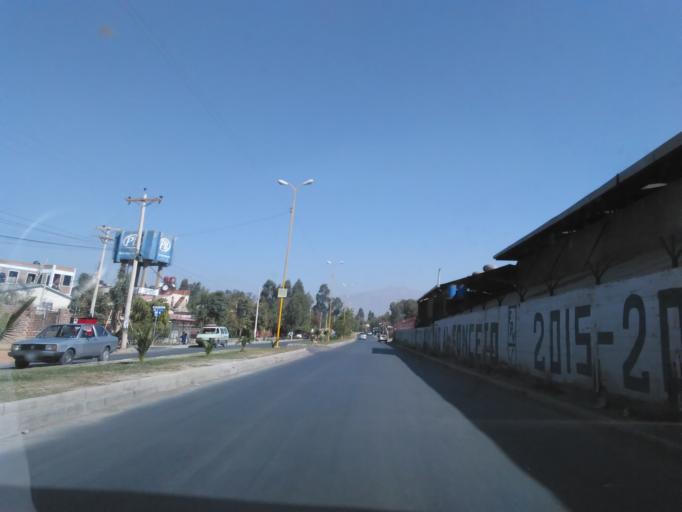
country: BO
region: Cochabamba
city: Cochabamba
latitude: -17.3934
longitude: -66.2650
